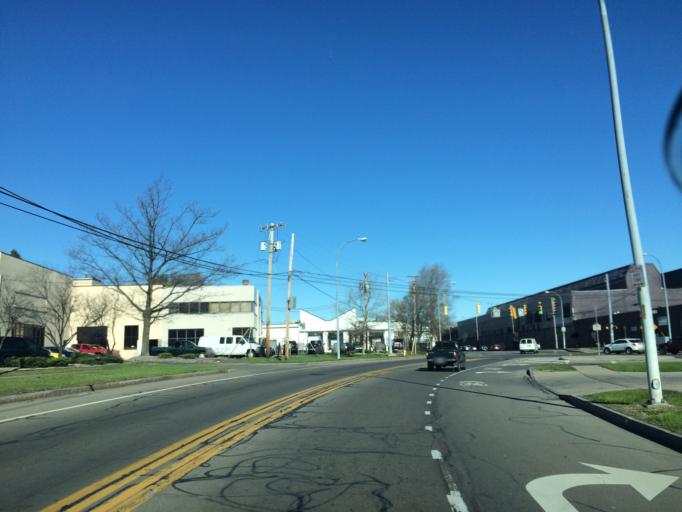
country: US
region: New York
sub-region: Monroe County
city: Brighton
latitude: 43.1492
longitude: -77.5639
